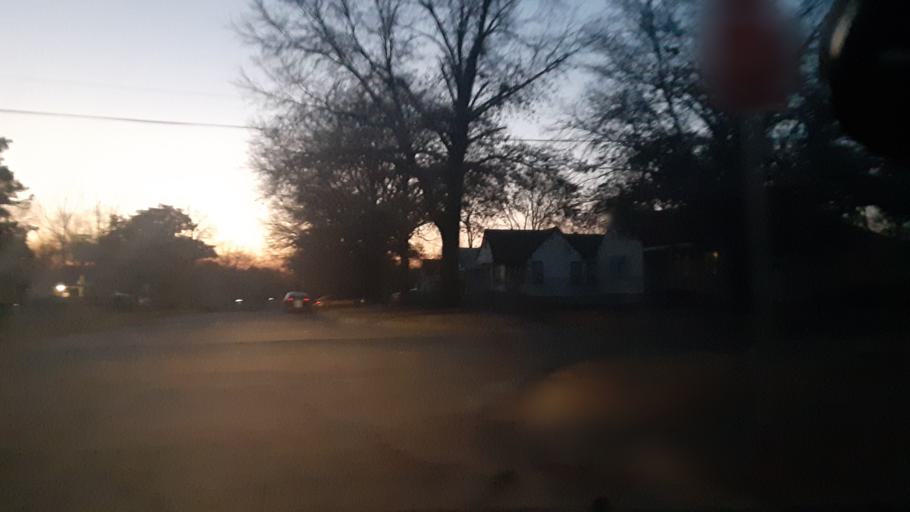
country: US
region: Oklahoma
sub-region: Payne County
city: Stillwater
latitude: 36.1113
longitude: -97.0666
